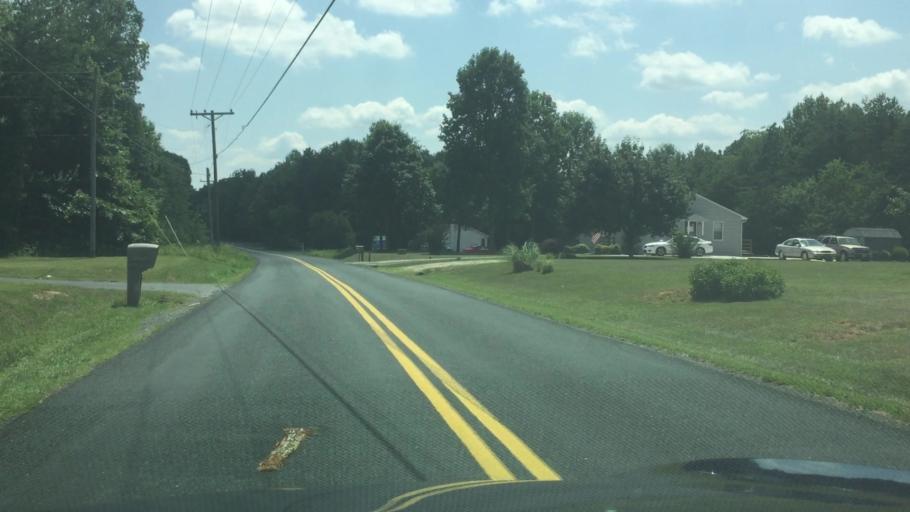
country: US
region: Virginia
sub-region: Appomattox County
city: Appomattox
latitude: 37.2969
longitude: -78.8501
